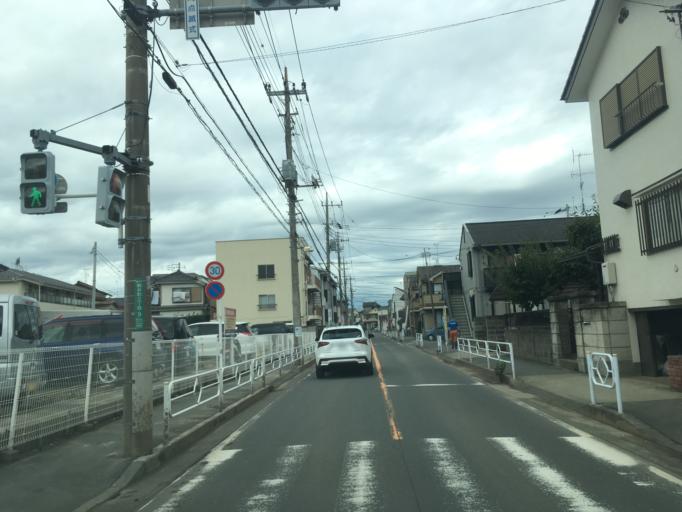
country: JP
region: Tokyo
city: Chofugaoka
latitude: 35.6229
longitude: 139.5836
